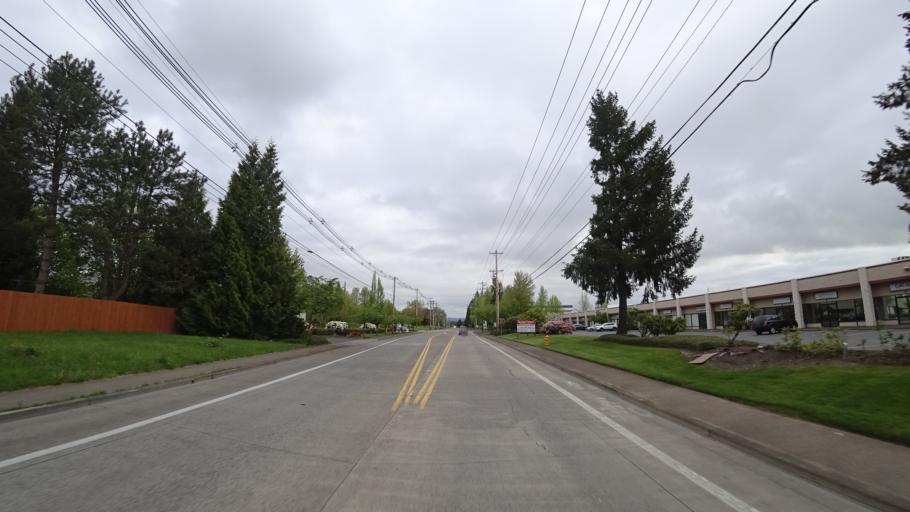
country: US
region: Oregon
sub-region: Washington County
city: Hillsboro
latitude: 45.5389
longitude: -122.9571
